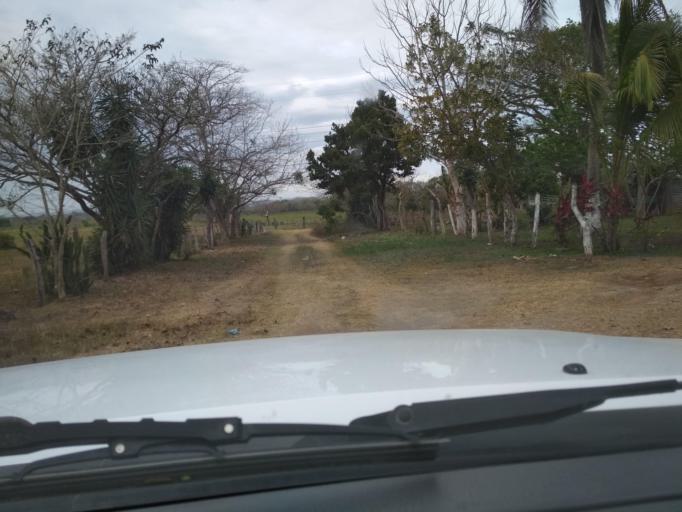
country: MX
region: Veracruz
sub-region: Veracruz
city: Delfino Victoria (Santa Fe)
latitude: 19.1610
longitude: -96.2958
